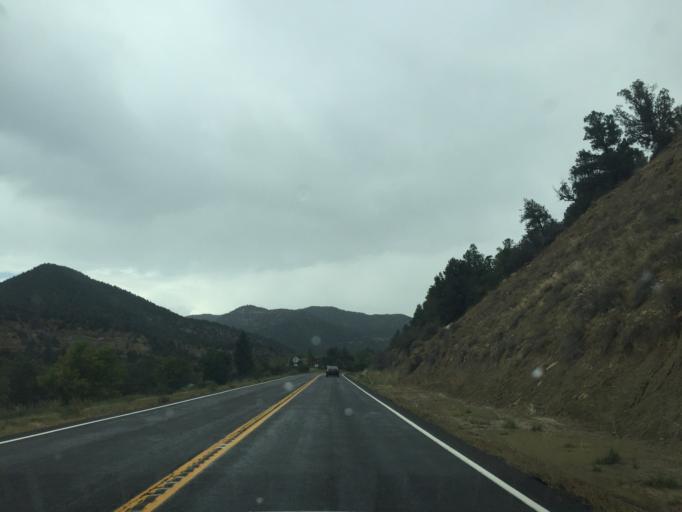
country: US
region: Utah
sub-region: Kane County
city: Kanab
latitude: 37.3248
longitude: -112.5992
